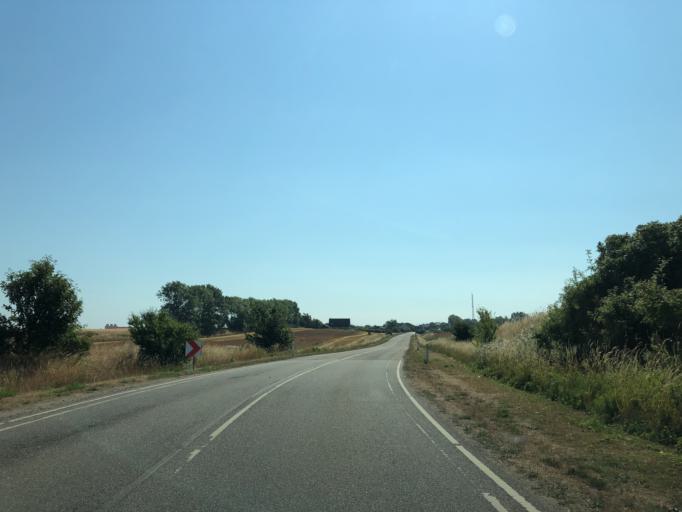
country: DK
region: Zealand
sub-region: Odsherred Kommune
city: Asnaes
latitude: 55.9737
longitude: 11.3499
